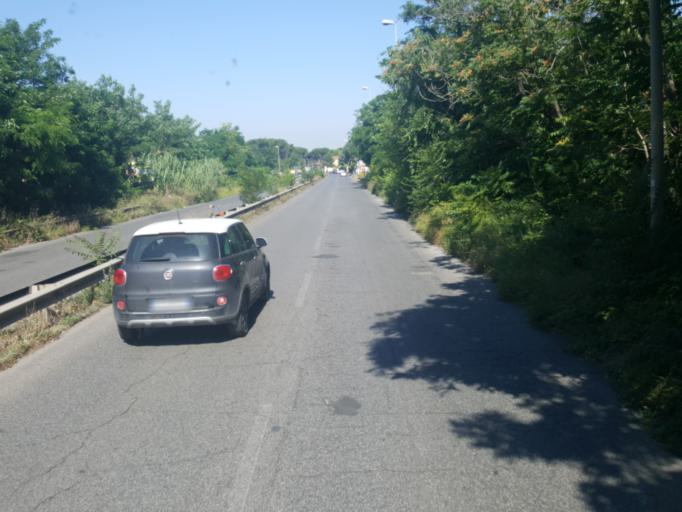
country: IT
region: Latium
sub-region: Citta metropolitana di Roma Capitale
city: Frascati
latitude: 41.8225
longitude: 12.6404
